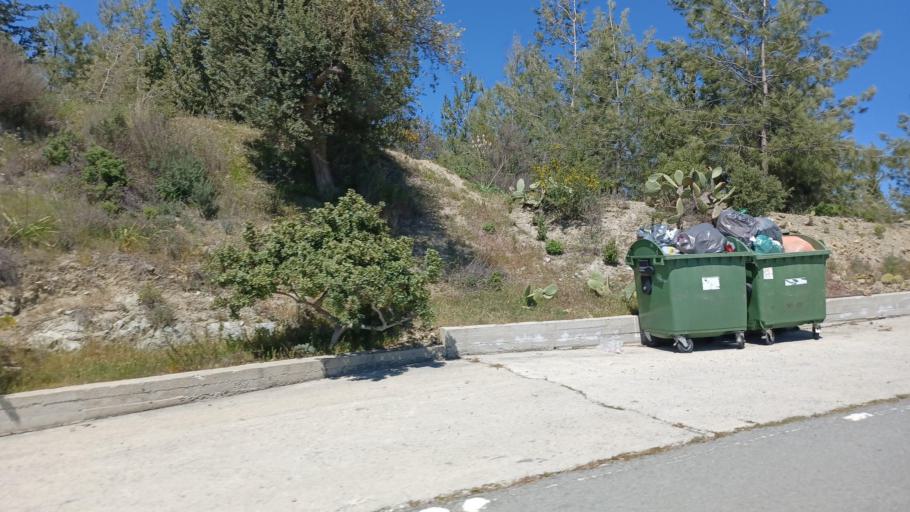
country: CY
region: Limassol
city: Parekklisha
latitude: 34.8070
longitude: 33.1429
